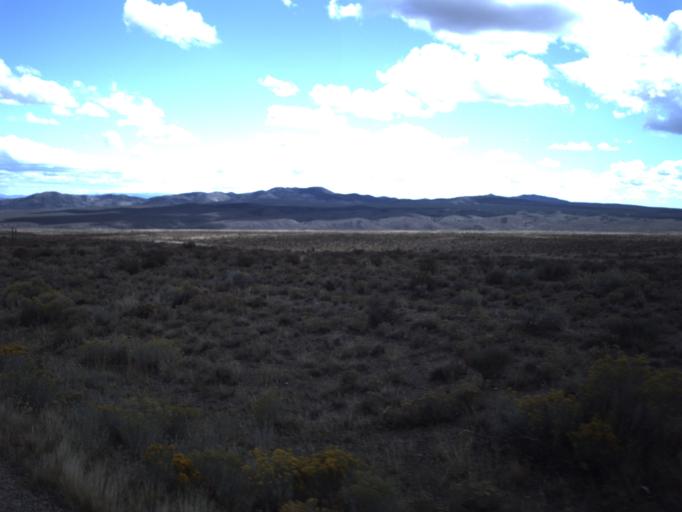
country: US
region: Utah
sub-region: Beaver County
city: Milford
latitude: 38.4536
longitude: -113.2091
